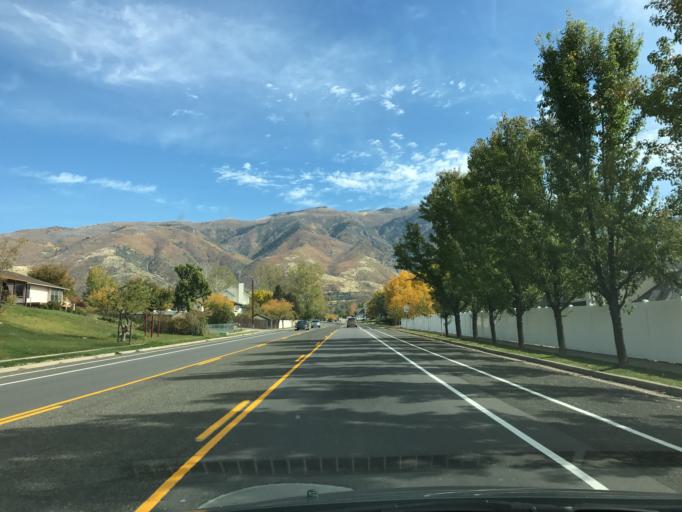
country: US
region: Utah
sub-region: Davis County
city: South Weber
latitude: 41.0890
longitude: -111.9321
